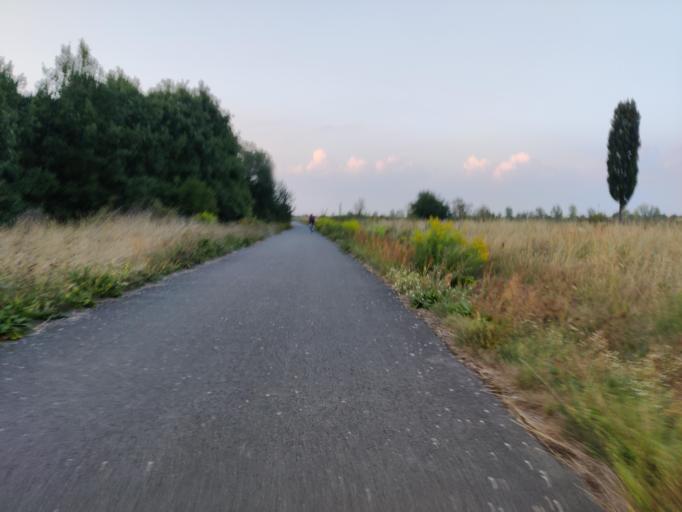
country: DE
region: Saxony
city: Zschortau
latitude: 51.4652
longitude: 12.3207
